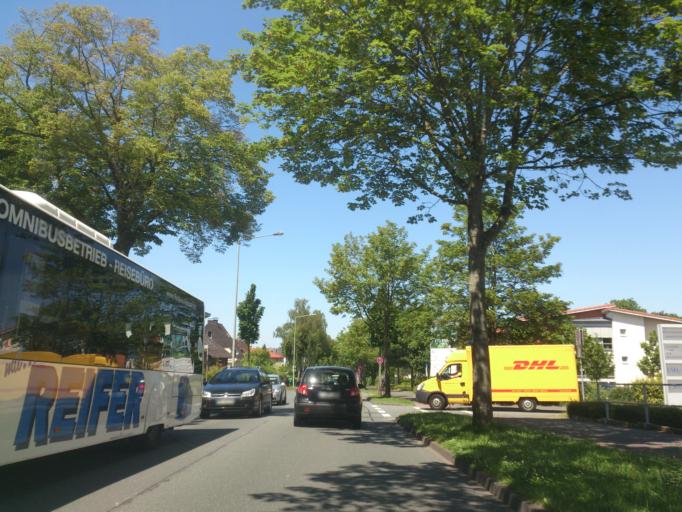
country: DE
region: North Rhine-Westphalia
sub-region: Regierungsbezirk Detmold
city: Paderborn
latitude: 51.7060
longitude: 8.7643
